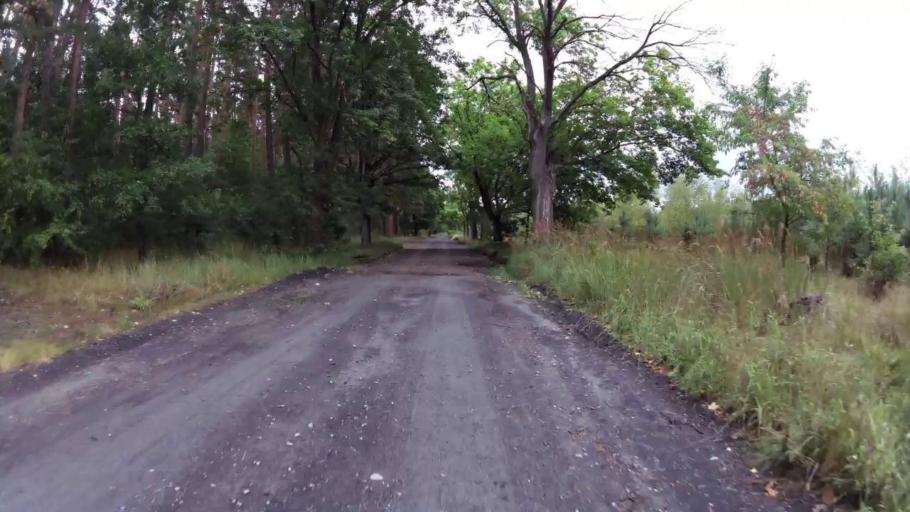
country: PL
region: West Pomeranian Voivodeship
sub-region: Powiat mysliborski
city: Debno
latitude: 52.8641
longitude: 14.7160
